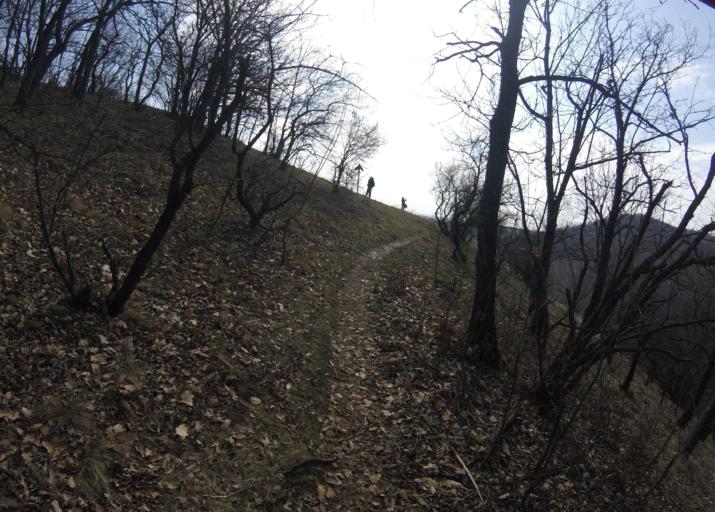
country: HU
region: Heves
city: Belapatfalva
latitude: 47.9946
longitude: 20.3283
